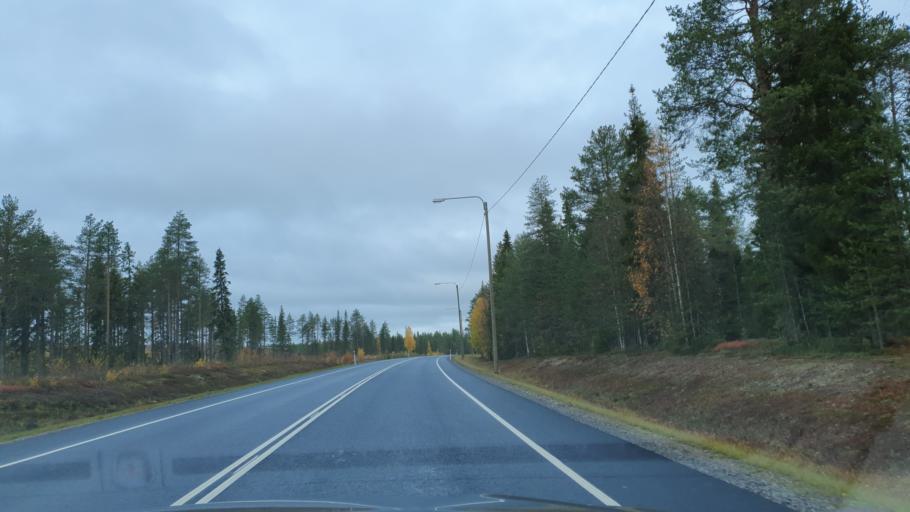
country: FI
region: Lapland
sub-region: Rovaniemi
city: Rovaniemi
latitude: 66.5363
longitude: 25.6616
